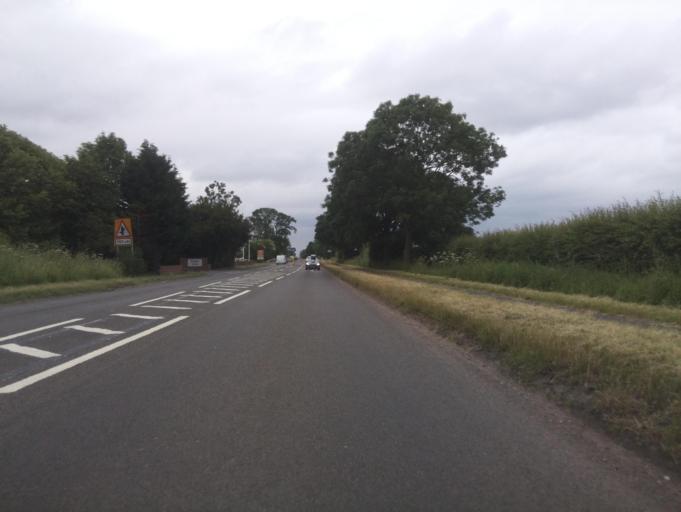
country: GB
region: England
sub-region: Staffordshire
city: Penkridge
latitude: 52.7457
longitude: -2.1076
